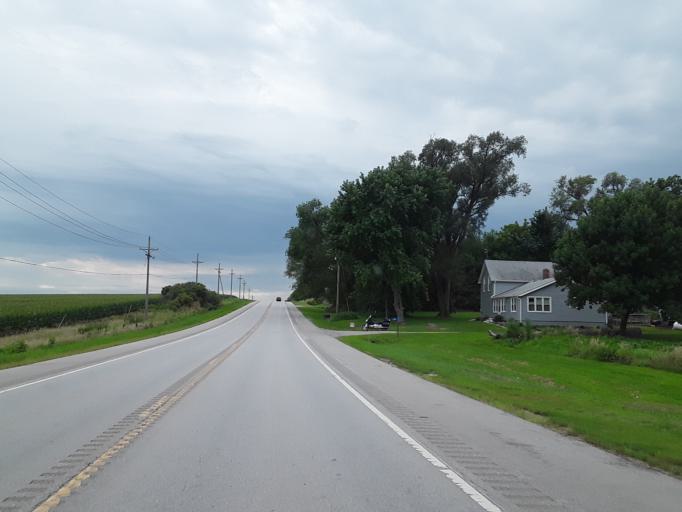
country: US
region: Nebraska
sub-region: Saunders County
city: Yutan
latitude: 41.2338
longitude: -96.3796
